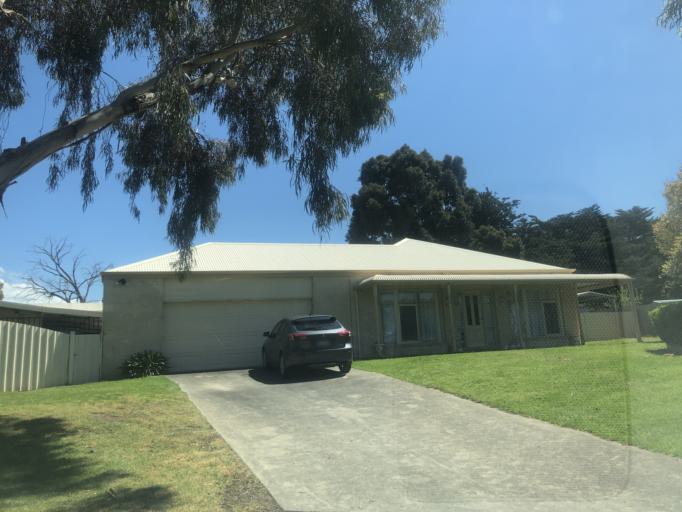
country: AU
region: Victoria
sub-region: Casey
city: Hallam
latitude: -37.9927
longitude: 145.2861
